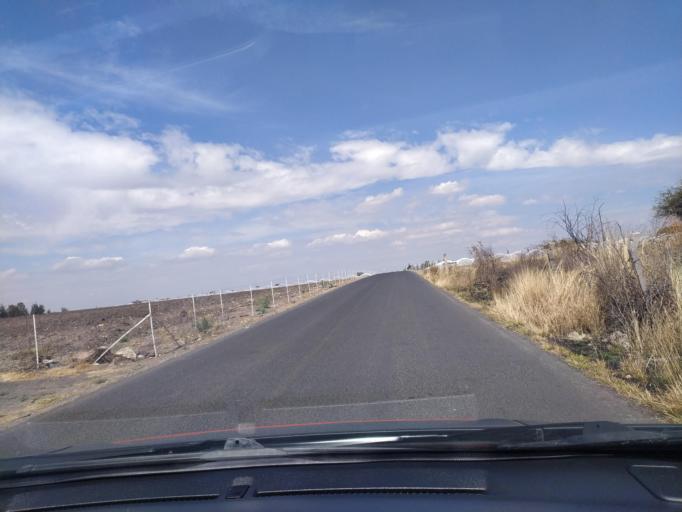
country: MX
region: Guanajuato
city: San Roque
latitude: 20.9592
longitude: -101.8301
